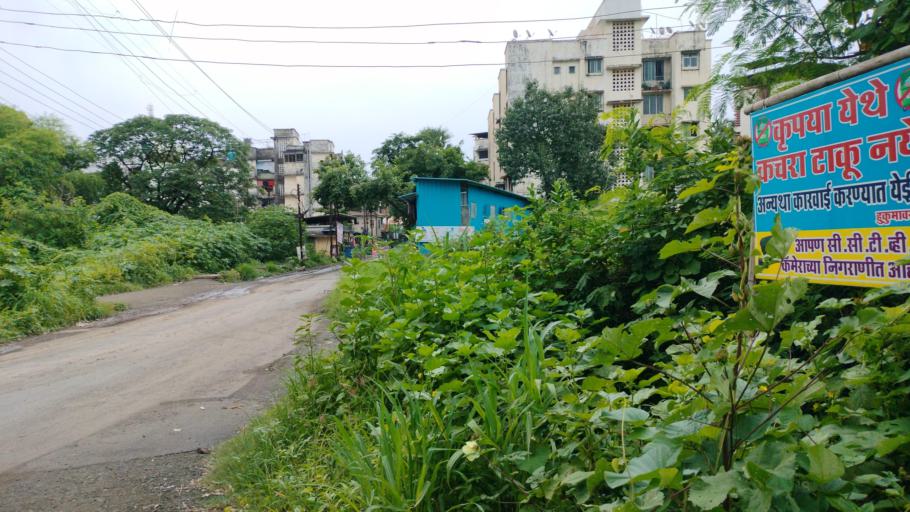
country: IN
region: Maharashtra
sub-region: Thane
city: Virar
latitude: 19.4386
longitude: 72.7942
